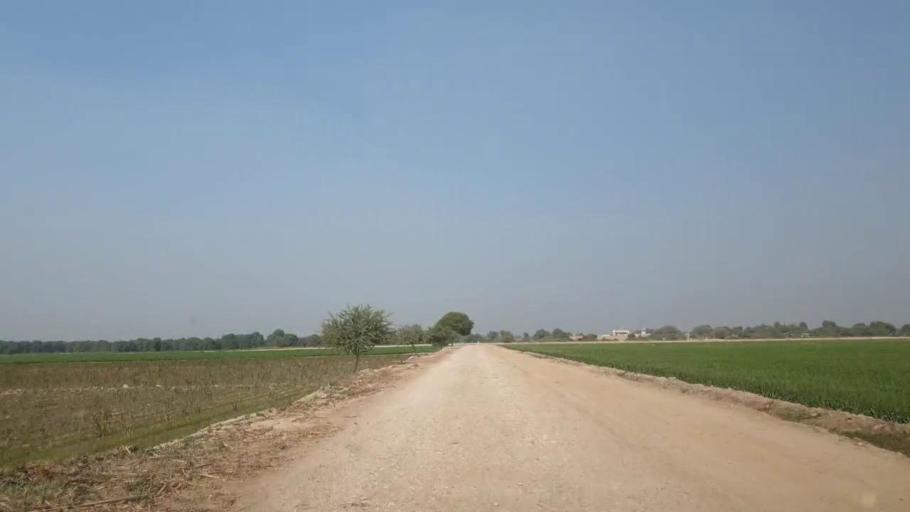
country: PK
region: Sindh
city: Tando Allahyar
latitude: 25.5007
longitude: 68.8340
